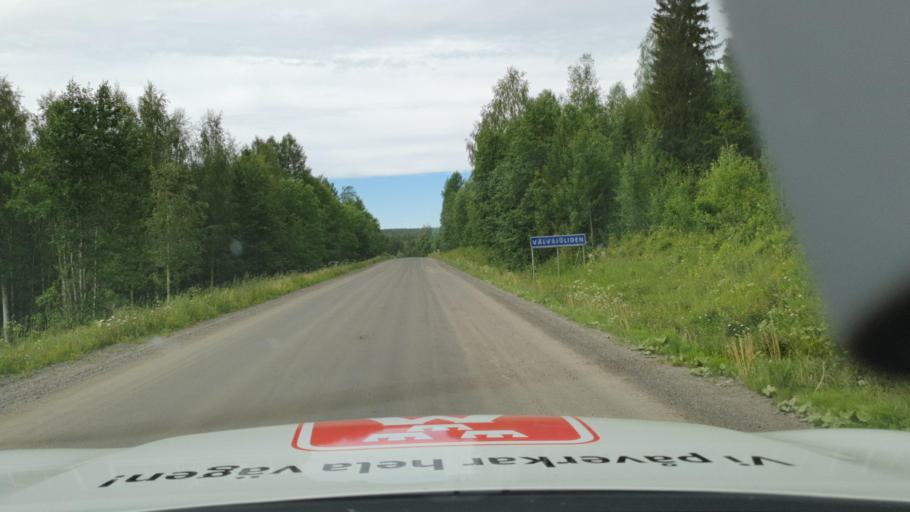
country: SE
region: Vaesterbotten
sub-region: Skelleftea Kommun
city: Burtraesk
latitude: 64.3598
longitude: 20.4273
